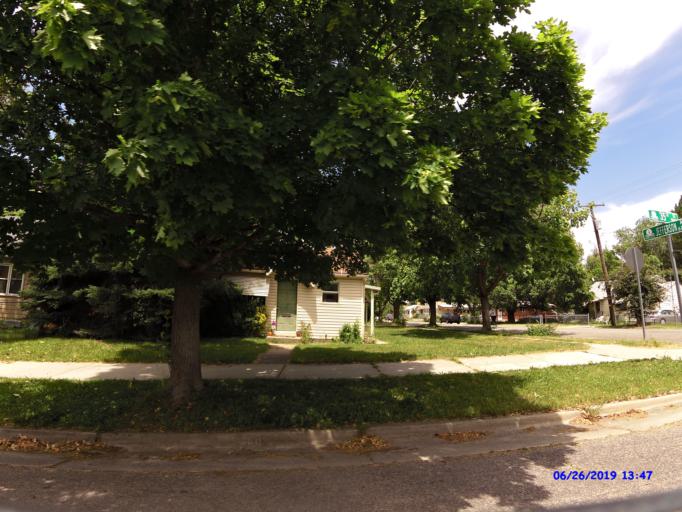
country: US
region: Utah
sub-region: Weber County
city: South Ogden
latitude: 41.1997
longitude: -111.9655
